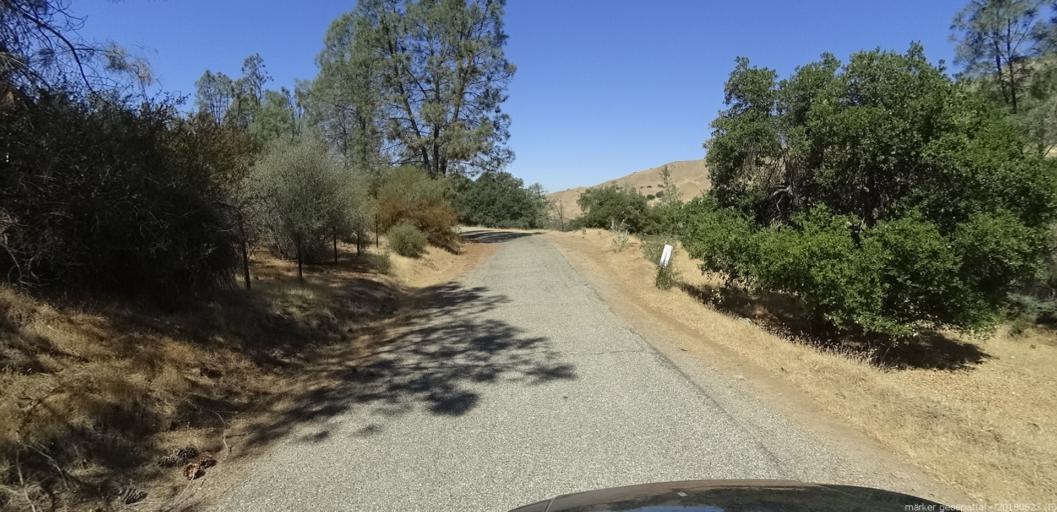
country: US
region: California
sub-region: Monterey County
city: King City
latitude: 36.2920
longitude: -120.8683
